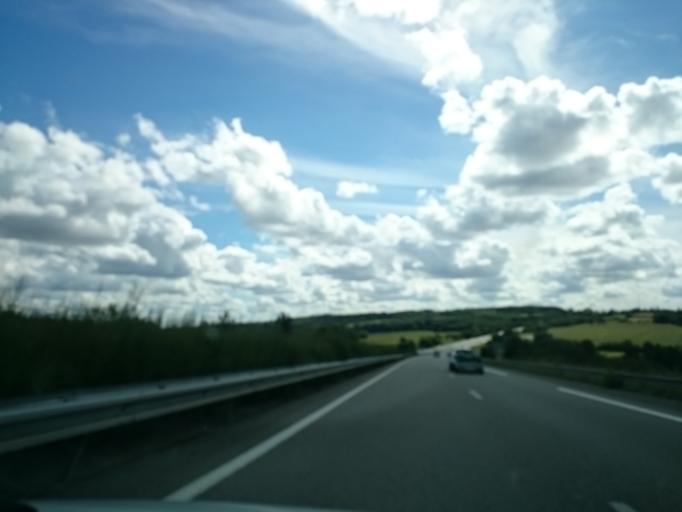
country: FR
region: Pays de la Loire
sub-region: Departement de la Loire-Atlantique
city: Mauves-sur-Loire
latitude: 47.3158
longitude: -1.4109
